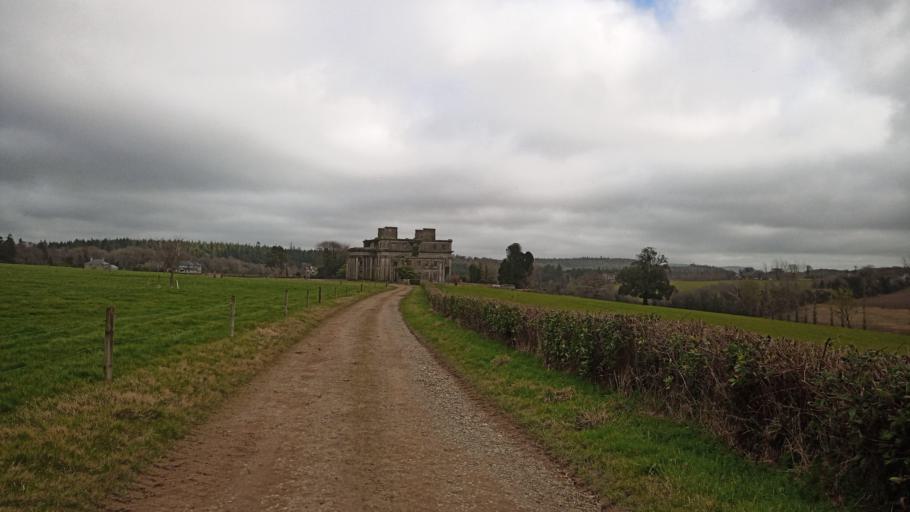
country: IE
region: Leinster
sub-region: Loch Garman
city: Enniscorthy
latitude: 52.4807
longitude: -6.7293
